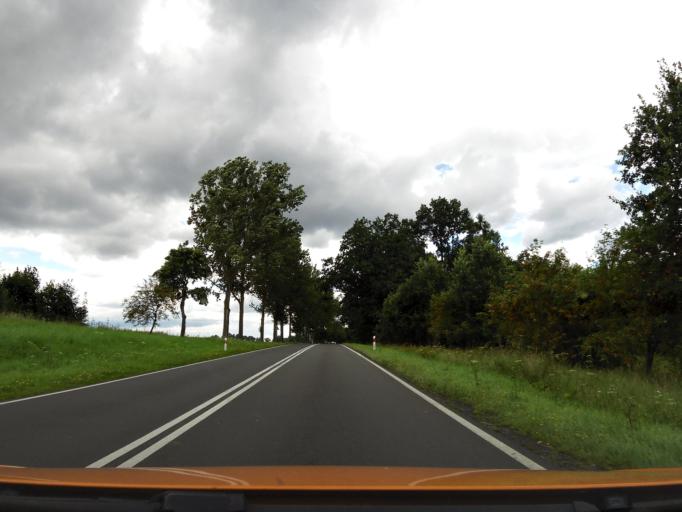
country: PL
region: West Pomeranian Voivodeship
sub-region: Powiat gryficki
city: Ploty
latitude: 53.7771
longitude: 15.2465
